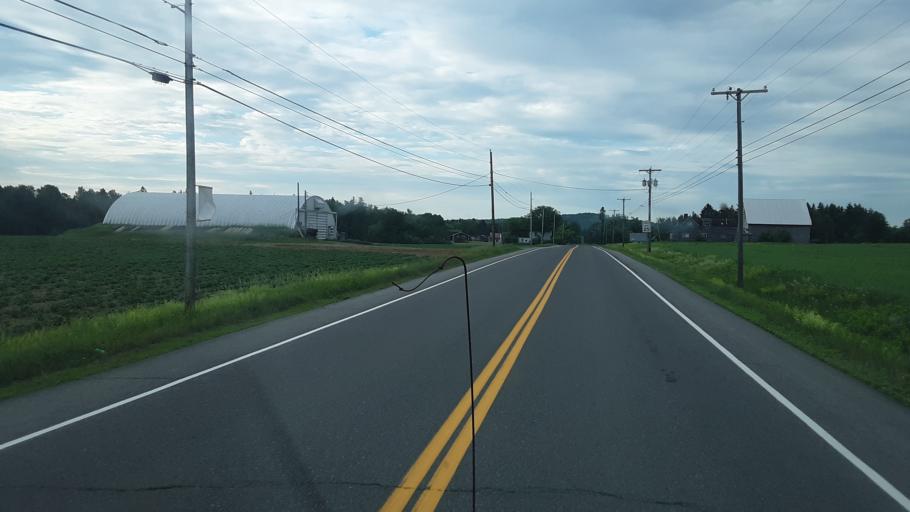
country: US
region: Maine
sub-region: Penobscot County
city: Patten
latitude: 45.9081
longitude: -68.4361
